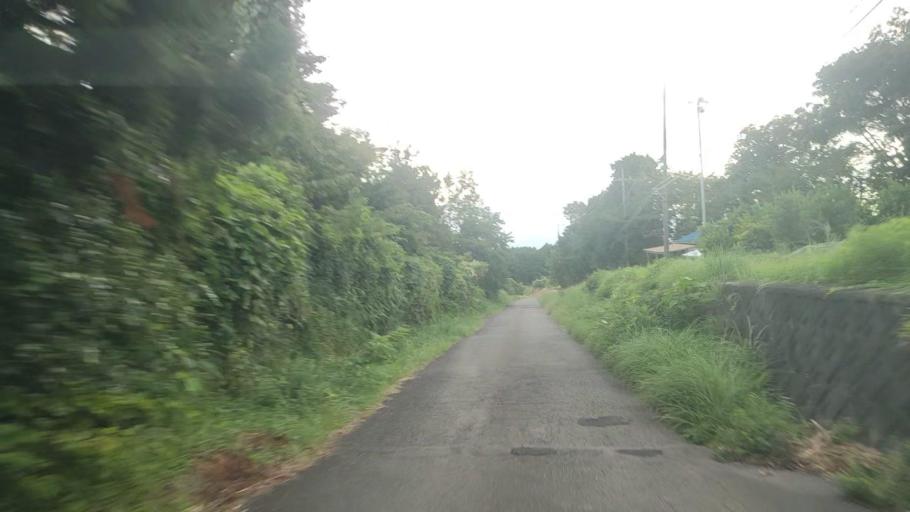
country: JP
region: Kanagawa
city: Hakone
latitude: 35.1269
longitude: 138.9909
